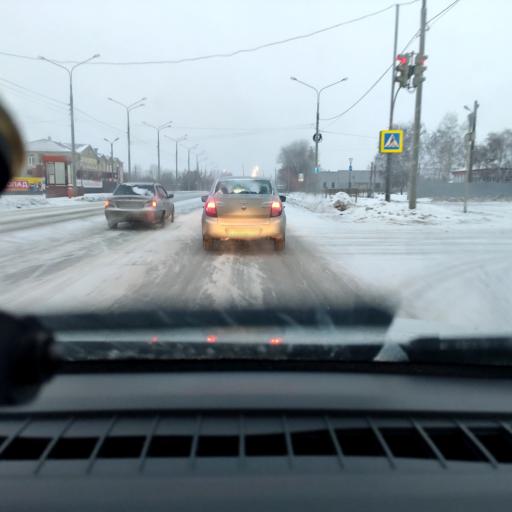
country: RU
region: Samara
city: Otradnyy
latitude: 53.3599
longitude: 51.3465
